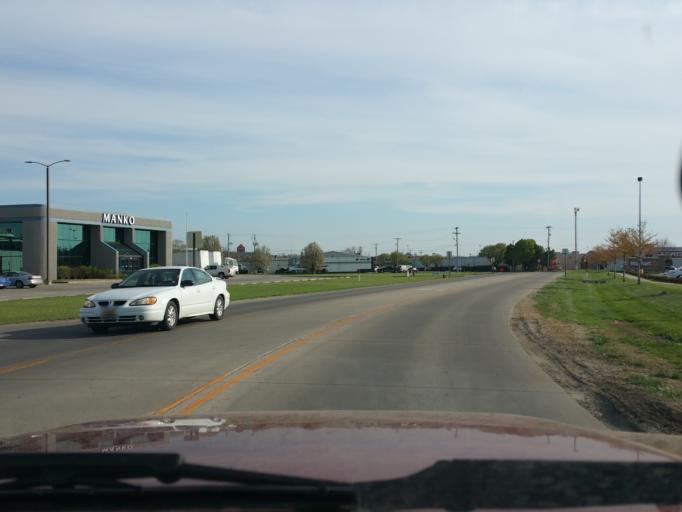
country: US
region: Kansas
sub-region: Riley County
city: Manhattan
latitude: 39.1873
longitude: -96.5549
